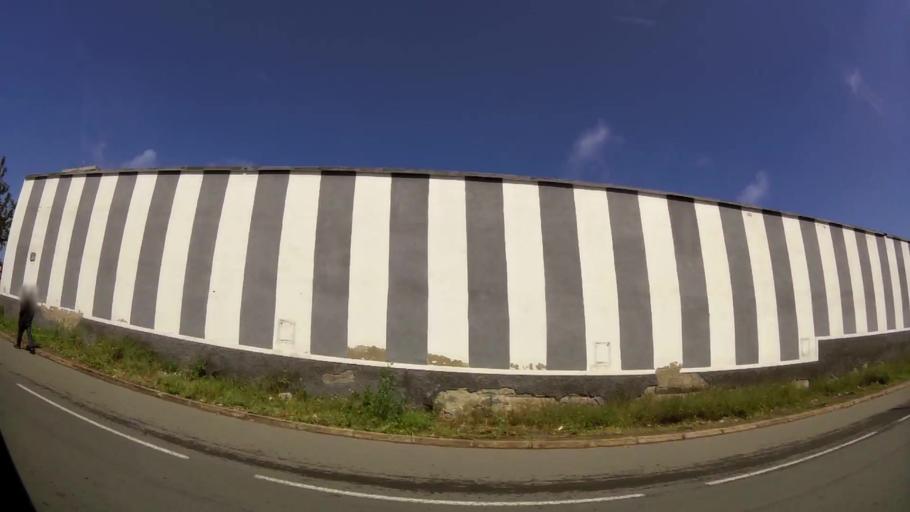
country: MA
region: Grand Casablanca
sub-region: Mediouna
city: Tit Mellil
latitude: 33.6161
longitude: -7.5212
